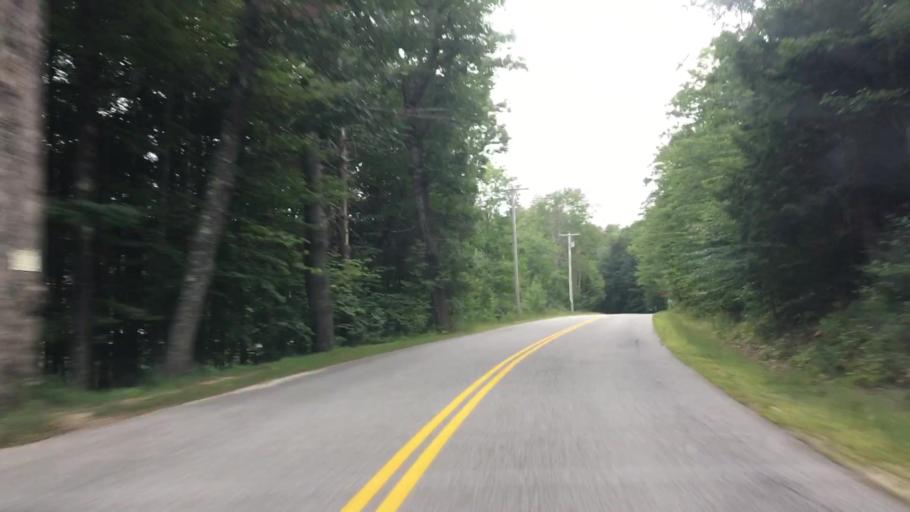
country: US
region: Maine
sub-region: Cumberland County
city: New Gloucester
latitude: 43.9200
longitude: -70.2544
